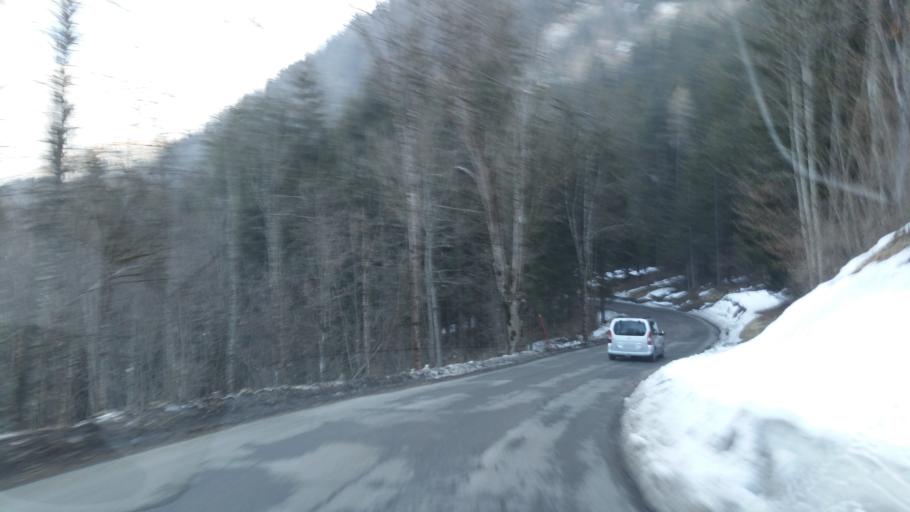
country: FR
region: Rhone-Alpes
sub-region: Departement de la Savoie
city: Saint-Jean-de-Maurienne
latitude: 45.2677
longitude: 6.3139
